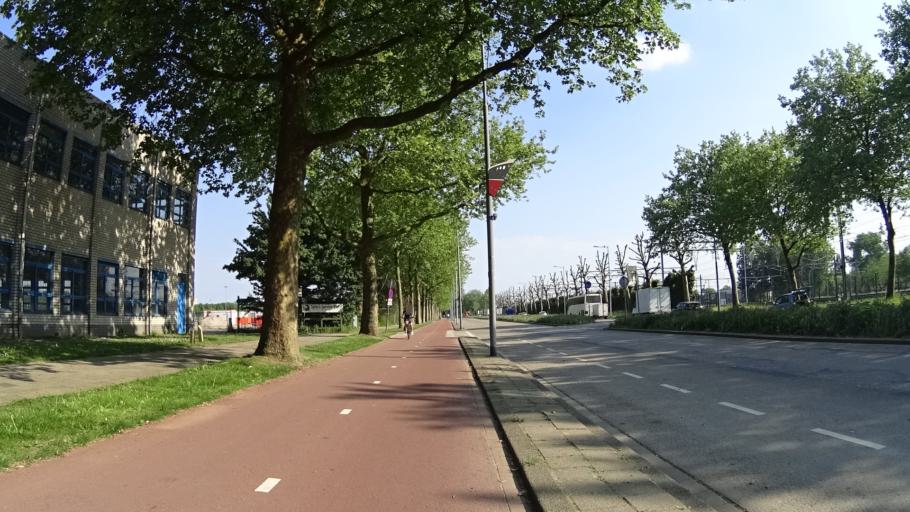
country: NL
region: South Holland
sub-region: Gemeente Barendrecht
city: Barendrecht
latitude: 51.8907
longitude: 4.5232
